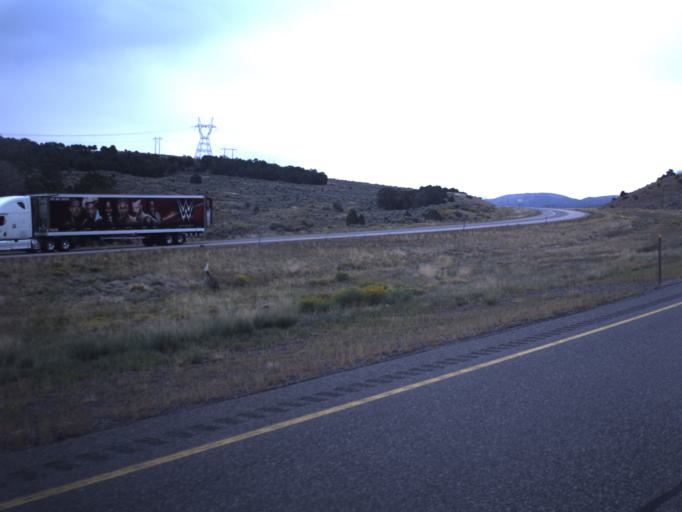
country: US
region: Utah
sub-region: Sevier County
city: Monroe
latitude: 38.5546
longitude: -112.4228
